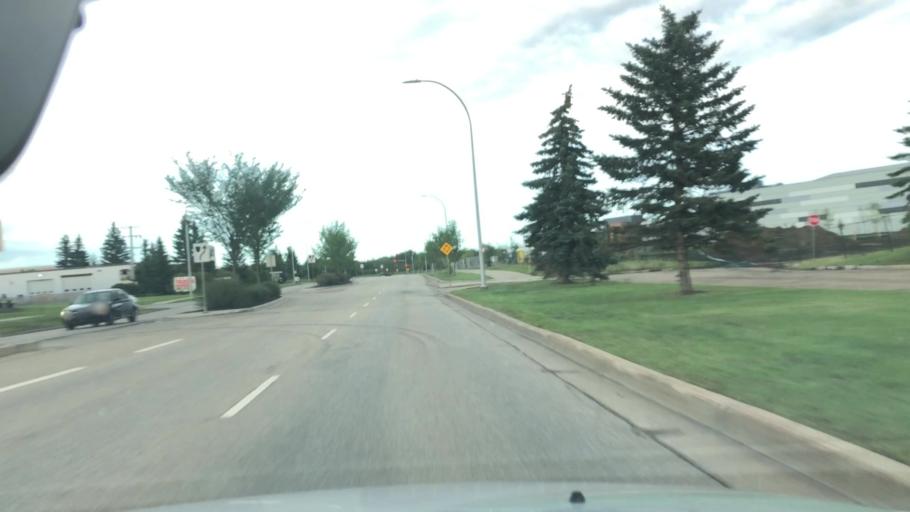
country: CA
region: Alberta
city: St. Albert
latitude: 53.6321
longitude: -113.5882
